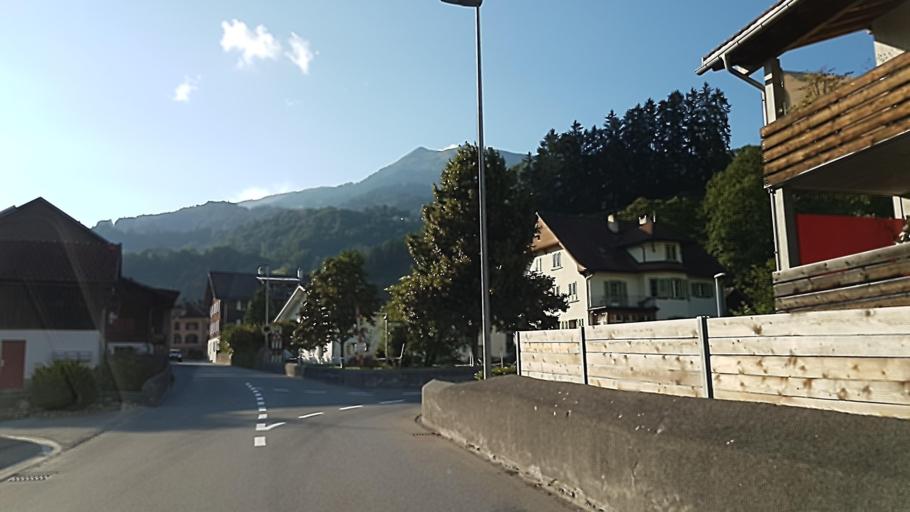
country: CH
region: Grisons
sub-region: Praettigau/Davos District
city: Grusch
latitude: 46.9801
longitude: 9.6519
